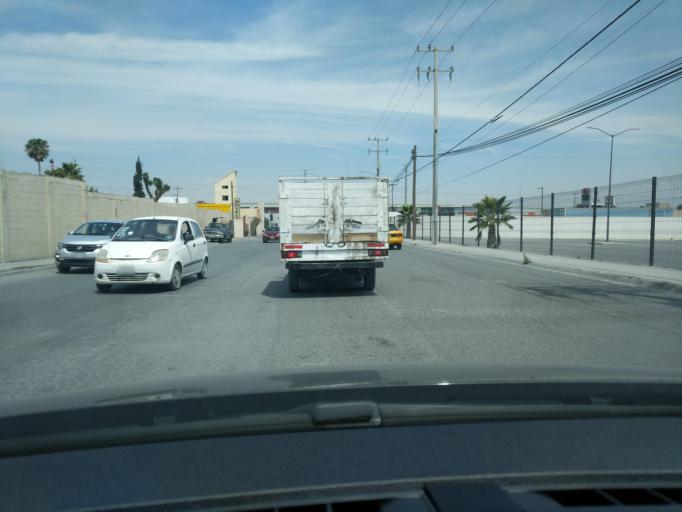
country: MX
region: Coahuila
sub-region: Arteaga
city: Arteaga
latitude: 25.4342
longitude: -100.9136
